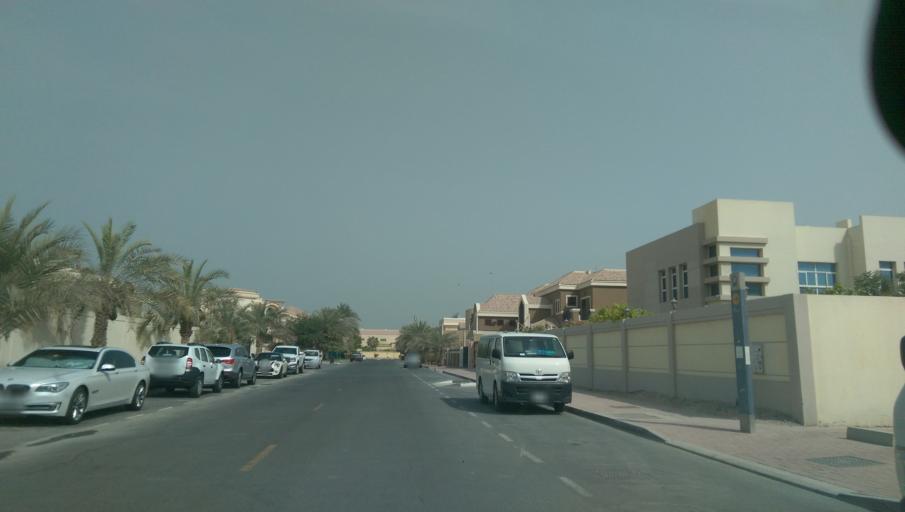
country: AE
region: Dubai
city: Dubai
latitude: 25.1566
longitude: 55.2253
